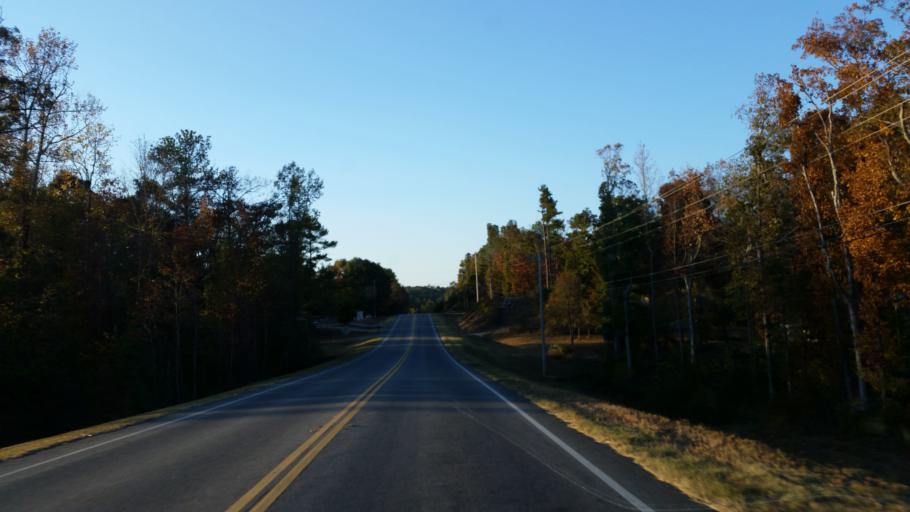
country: US
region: Georgia
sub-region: Gordon County
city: Calhoun
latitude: 34.5202
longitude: -84.9675
